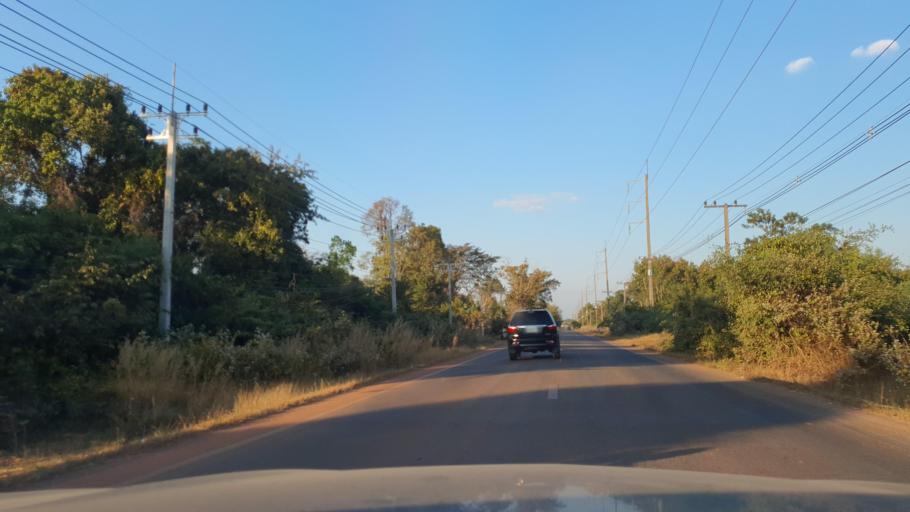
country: TH
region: Nakhon Phanom
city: Si Songkhram
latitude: 17.5976
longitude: 104.2379
